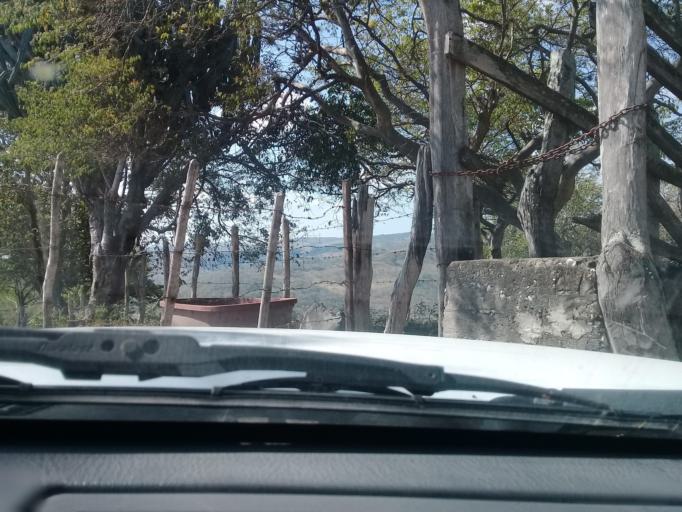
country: MX
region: Veracruz
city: Actopan
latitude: 19.4827
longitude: -96.6493
